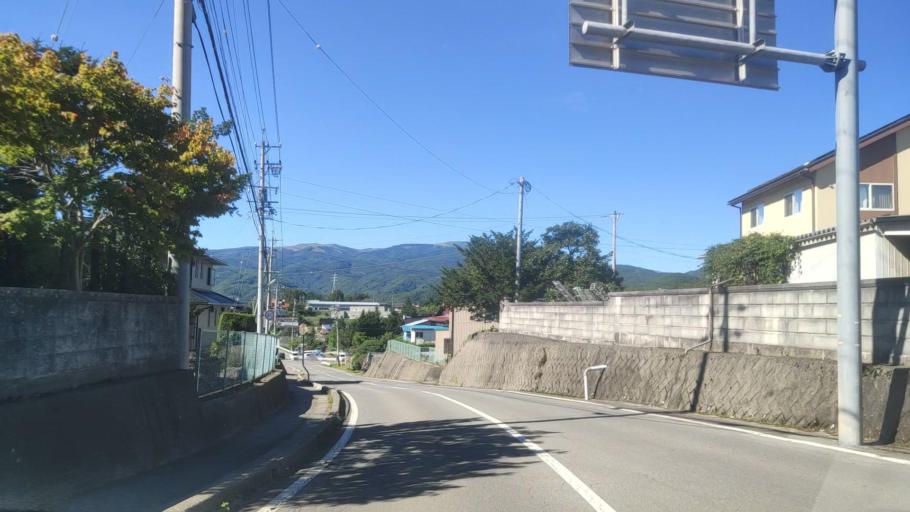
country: JP
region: Nagano
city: Chino
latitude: 36.0179
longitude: 138.2071
